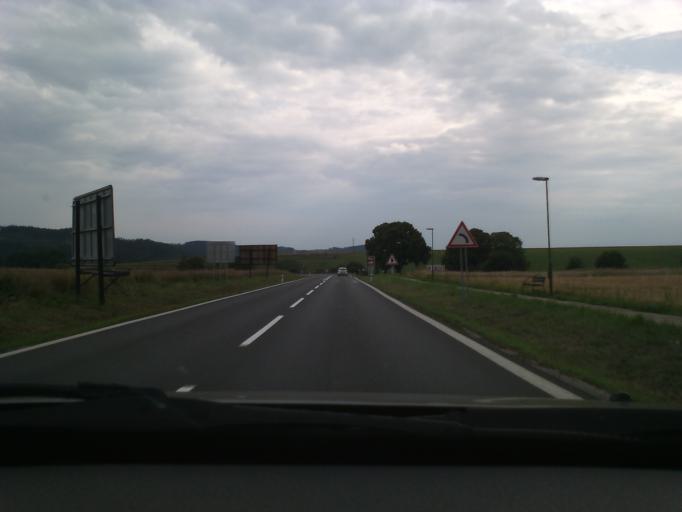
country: SK
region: Presovsky
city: Spisska Bela
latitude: 49.1804
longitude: 20.4514
